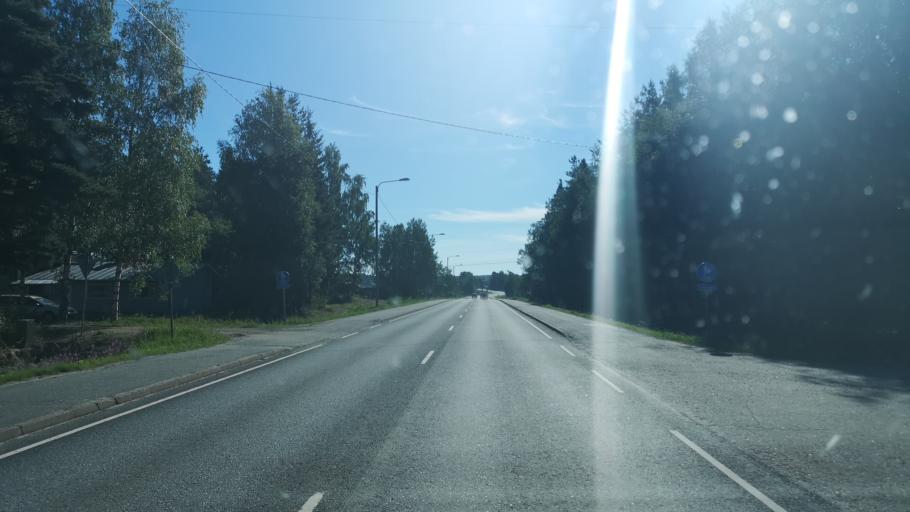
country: FI
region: Southern Ostrobothnia
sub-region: Seinaejoki
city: Lapua
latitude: 62.9696
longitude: 23.0650
